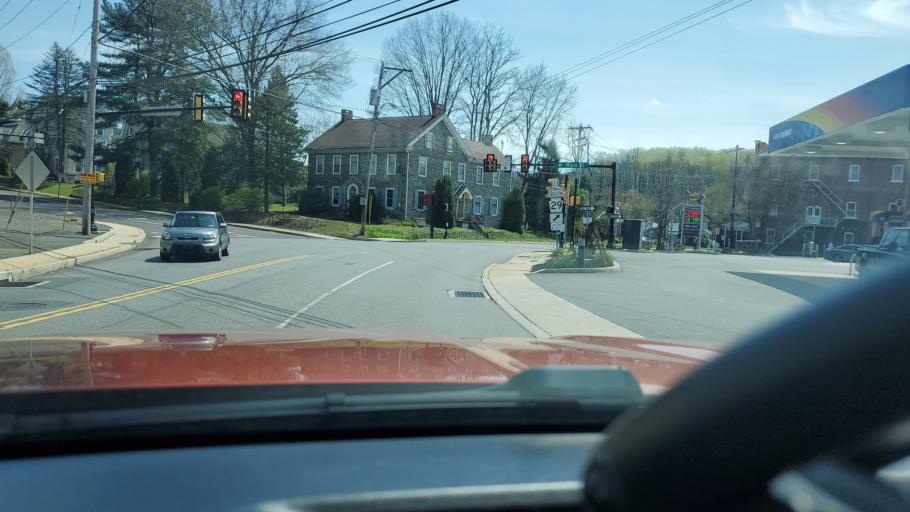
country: US
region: Pennsylvania
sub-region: Montgomery County
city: Red Hill
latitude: 40.3394
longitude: -75.4717
